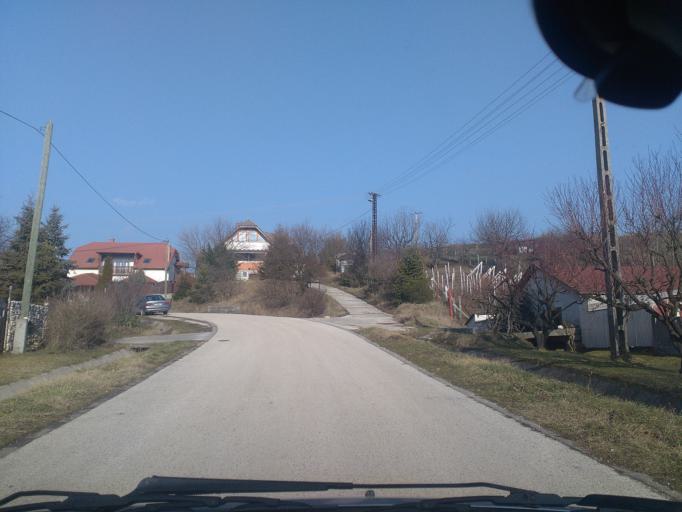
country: HU
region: Komarom-Esztergom
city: Piliscsev
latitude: 47.6827
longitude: 18.8130
